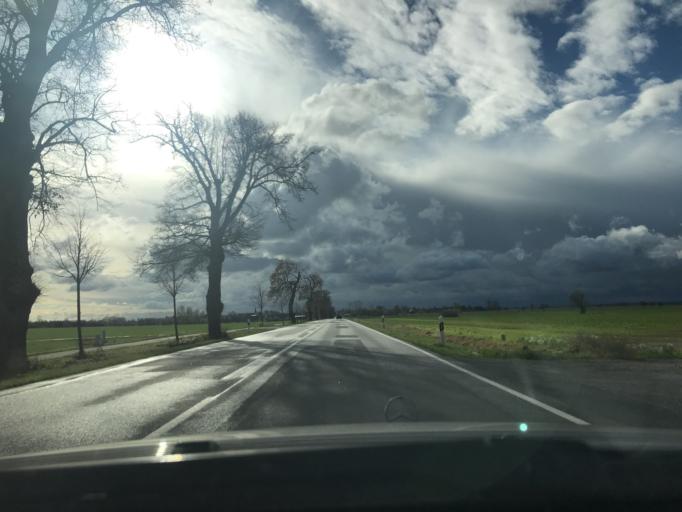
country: DE
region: Mecklenburg-Vorpommern
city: Jarmen
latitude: 53.8902
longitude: 13.3380
